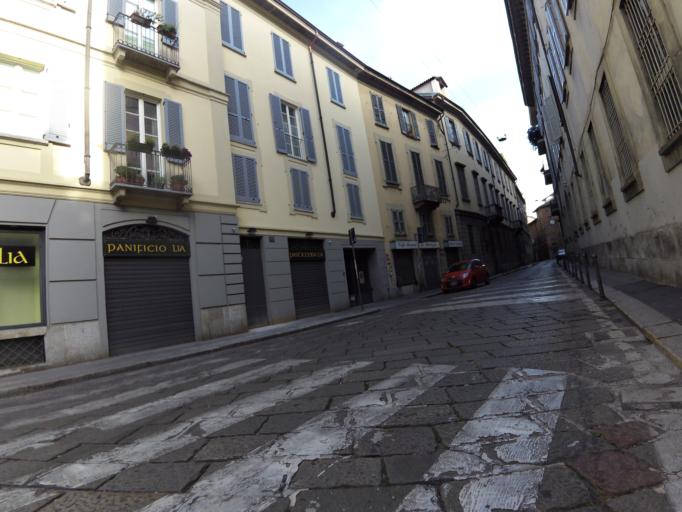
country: IT
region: Lombardy
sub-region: Citta metropolitana di Milano
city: Milano
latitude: 45.4640
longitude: 9.1793
